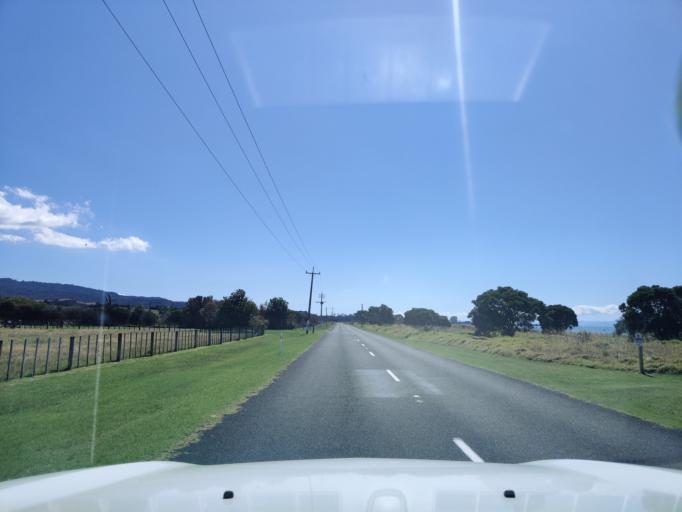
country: NZ
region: Waikato
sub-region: Thames-Coromandel District
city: Thames
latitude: -37.0741
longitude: 175.2959
